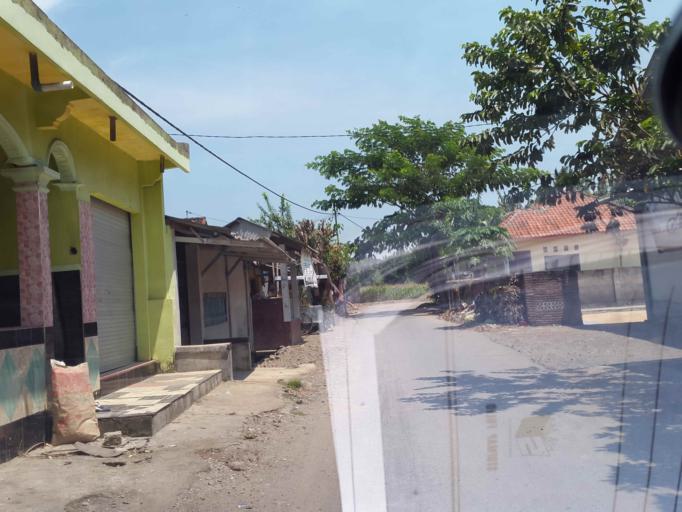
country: ID
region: West Nusa Tenggara
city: Karangkebon Timur
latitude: -8.6565
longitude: 116.1139
